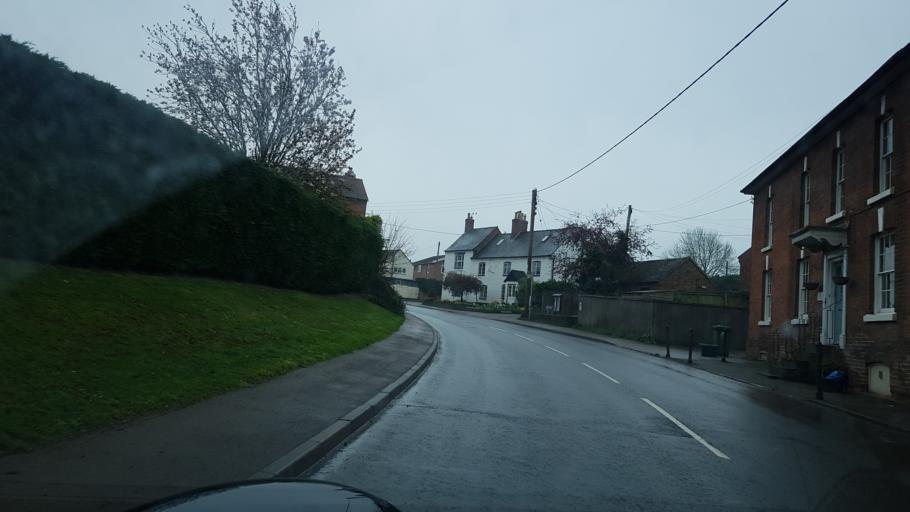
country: GB
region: England
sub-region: Herefordshire
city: Donnington
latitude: 51.9791
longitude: -2.4398
